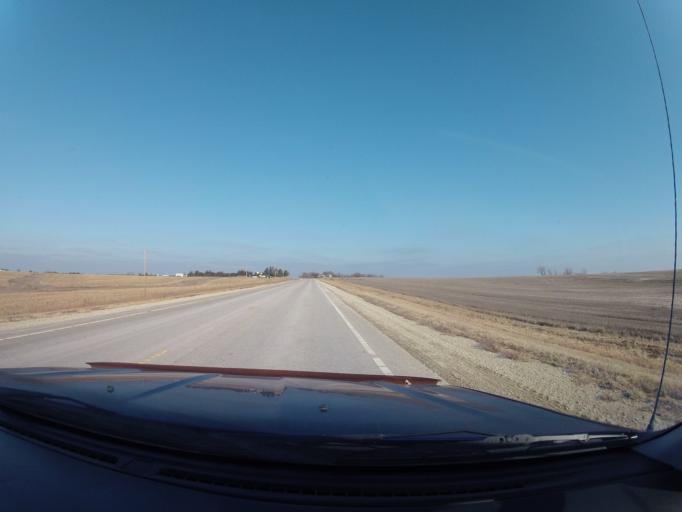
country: US
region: Kansas
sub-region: Marshall County
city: Blue Rapids
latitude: 39.5899
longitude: -96.7501
